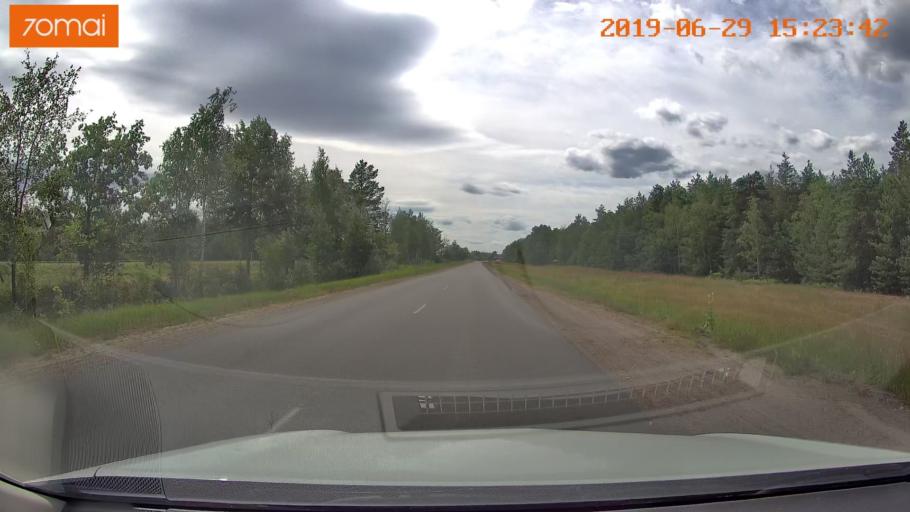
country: BY
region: Brest
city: Mikashevichy
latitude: 52.2110
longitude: 27.4291
